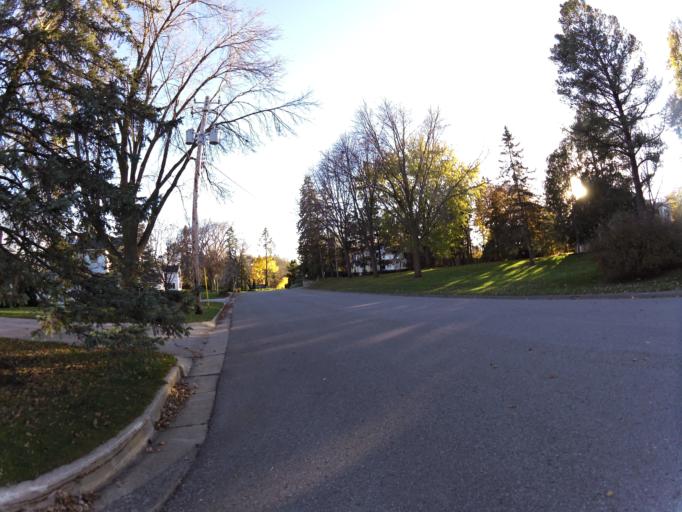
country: US
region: Minnesota
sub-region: Olmsted County
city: Rochester
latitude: 44.0155
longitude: -92.4810
